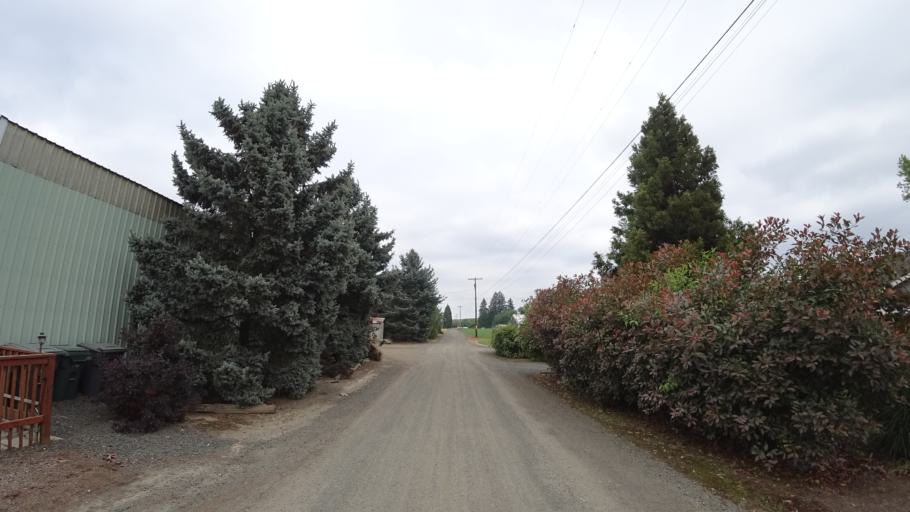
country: US
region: Oregon
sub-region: Washington County
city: Hillsboro
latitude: 45.4946
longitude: -122.9912
